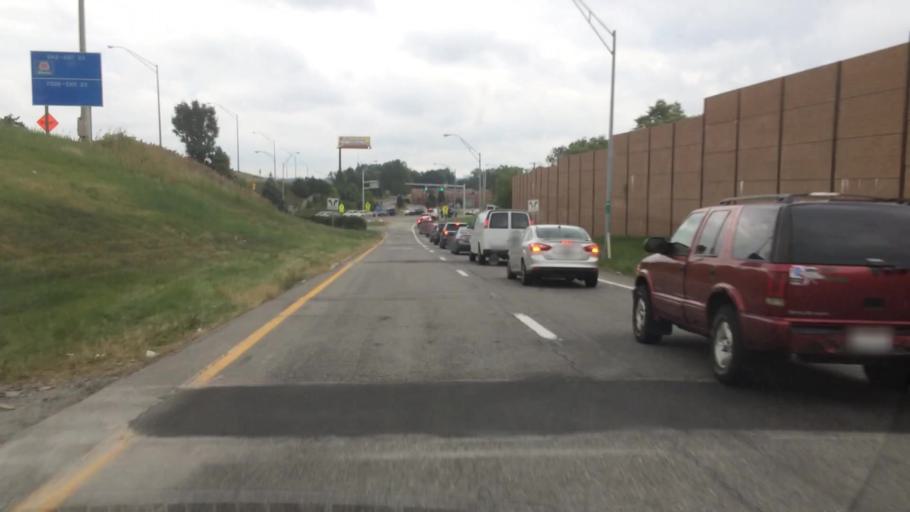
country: US
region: Ohio
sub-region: Cuyahoga County
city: Garfield Heights
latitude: 41.4156
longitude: -81.5957
